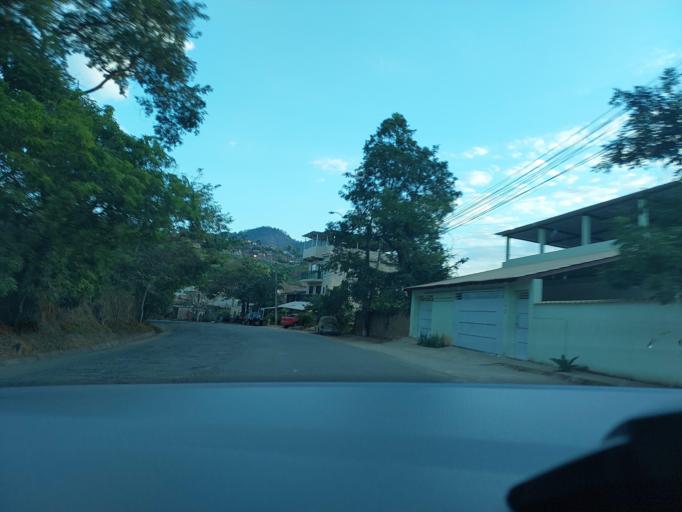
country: BR
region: Rio de Janeiro
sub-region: Natividade
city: Natividade
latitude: -21.2009
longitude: -42.1240
